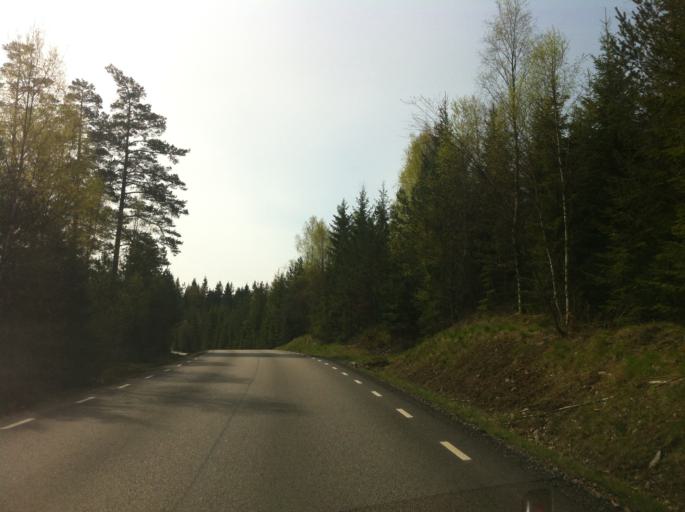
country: SE
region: Vaestra Goetaland
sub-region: Marks Kommun
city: Fritsla
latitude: 57.3763
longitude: 12.8601
